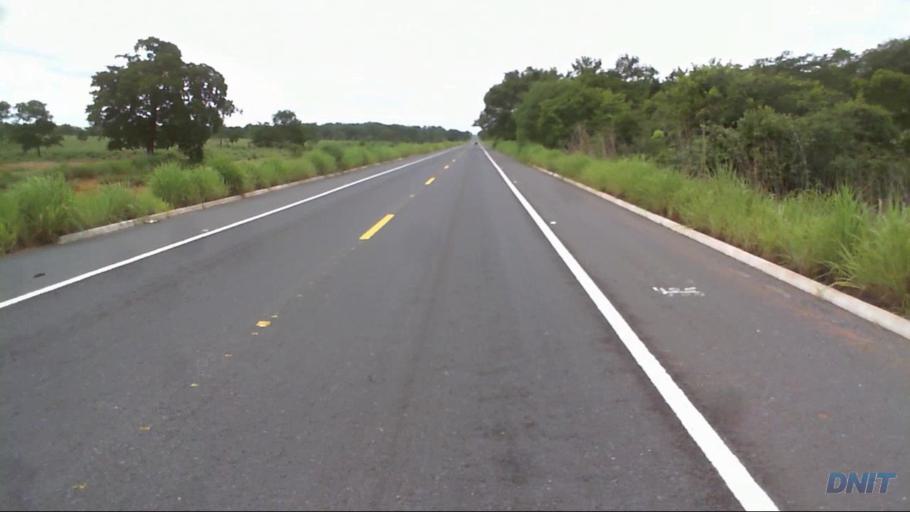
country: BR
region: Goias
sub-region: Sao Miguel Do Araguaia
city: Sao Miguel do Araguaia
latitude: -13.2630
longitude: -50.5147
